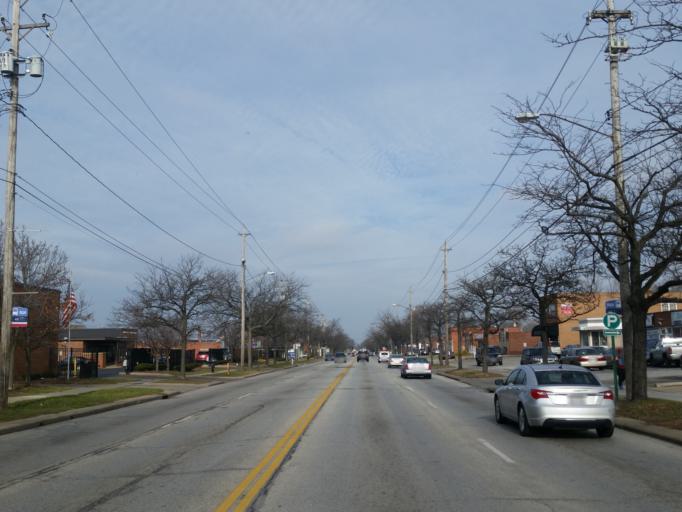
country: US
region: Ohio
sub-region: Cuyahoga County
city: Shaker Heights
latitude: 41.4594
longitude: -81.5649
